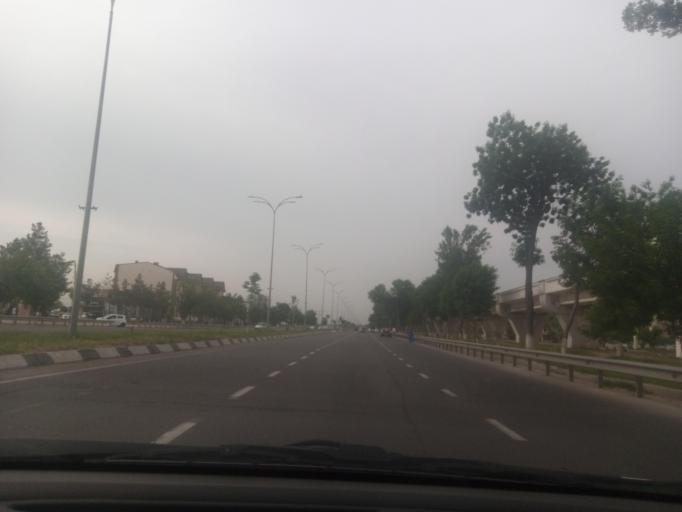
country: UZ
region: Toshkent Shahri
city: Bektemir
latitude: 41.2879
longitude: 69.3597
